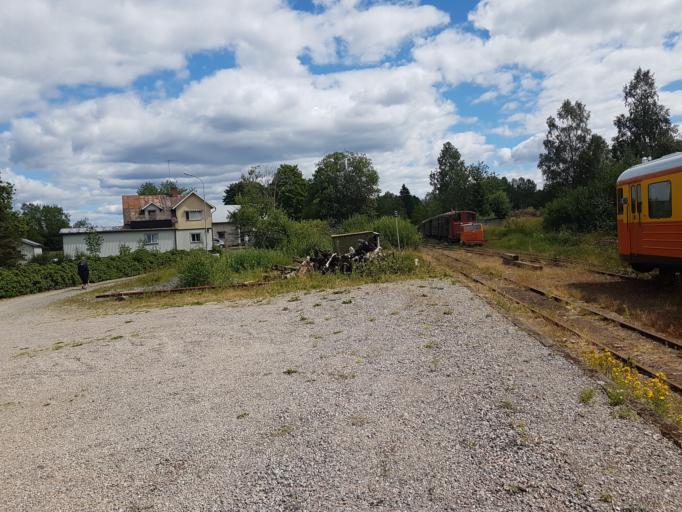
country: SE
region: Kronoberg
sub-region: Uppvidinge Kommun
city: Aseda
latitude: 57.2150
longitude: 15.4377
